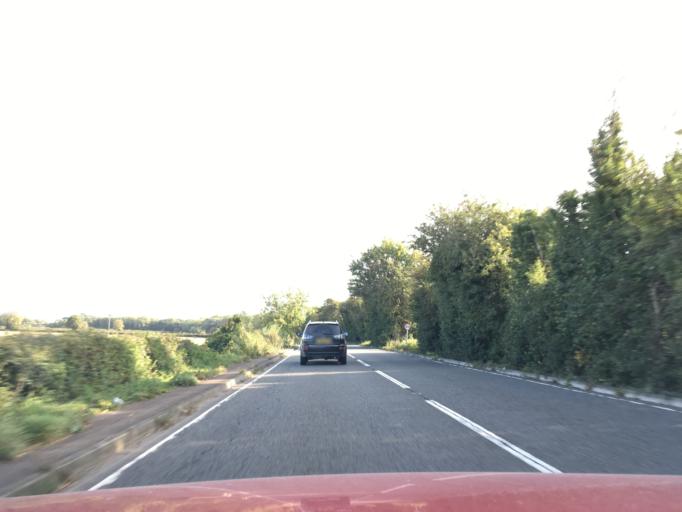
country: GB
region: England
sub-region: Gloucestershire
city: Gloucester
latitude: 51.8820
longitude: -2.2673
